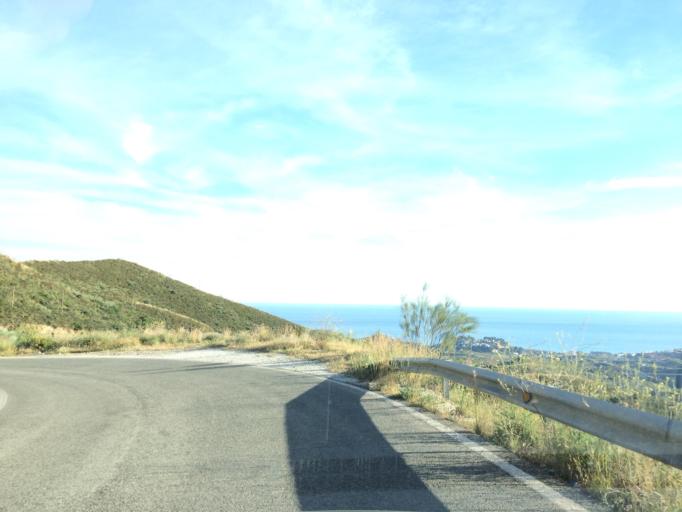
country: ES
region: Andalusia
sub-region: Provincia de Malaga
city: Totalan
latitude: 36.7454
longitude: -4.3301
